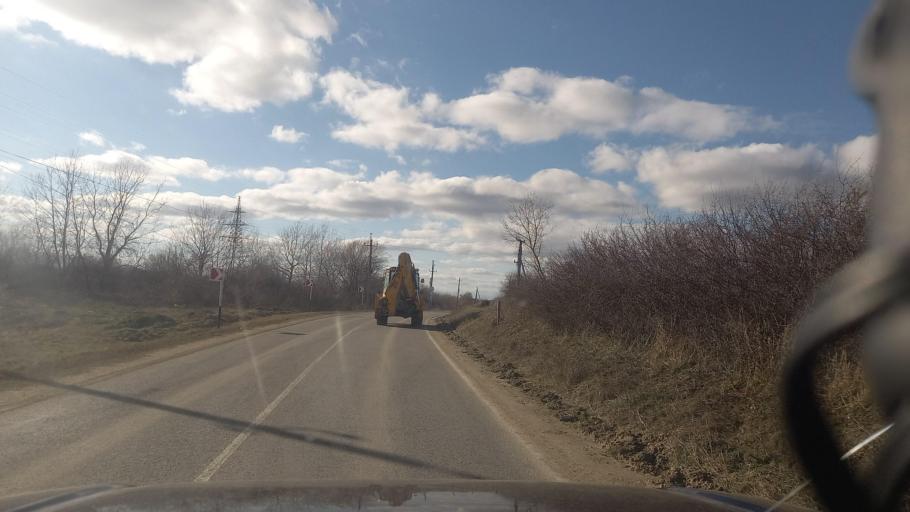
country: RU
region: Adygeya
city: Yablonovskiy
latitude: 45.0183
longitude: 38.9044
